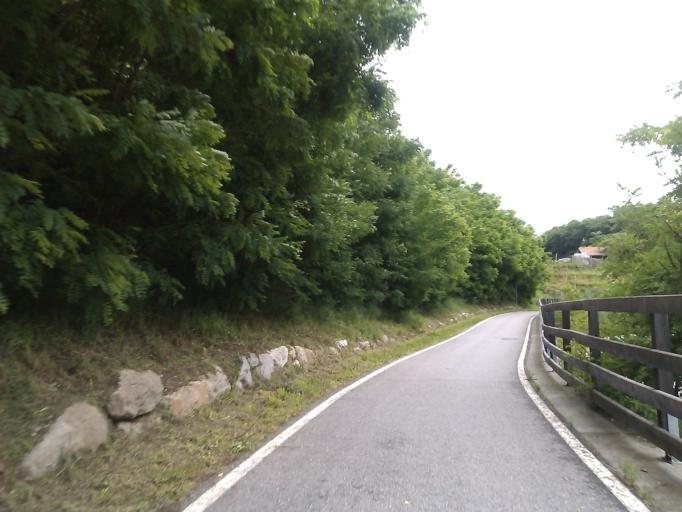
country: IT
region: Trentino-Alto Adige
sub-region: Bolzano
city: Laces
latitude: 46.6231
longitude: 10.8699
